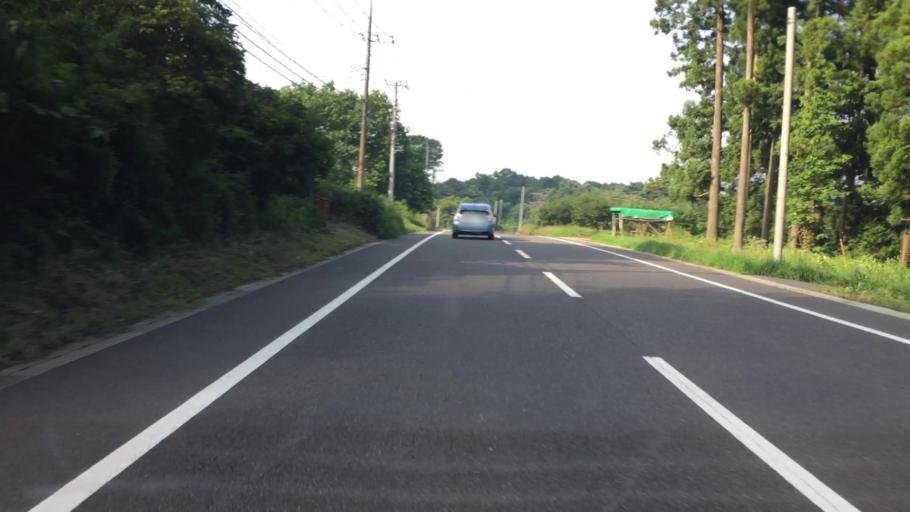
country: JP
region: Tochigi
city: Kuroiso
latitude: 37.0765
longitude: 140.0494
